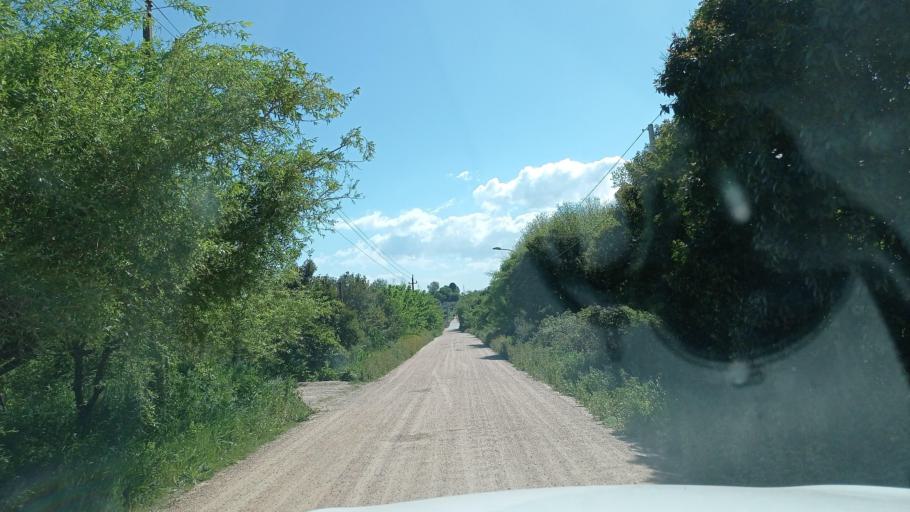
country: UY
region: Canelones
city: Toledo
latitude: -34.7798
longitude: -56.1513
